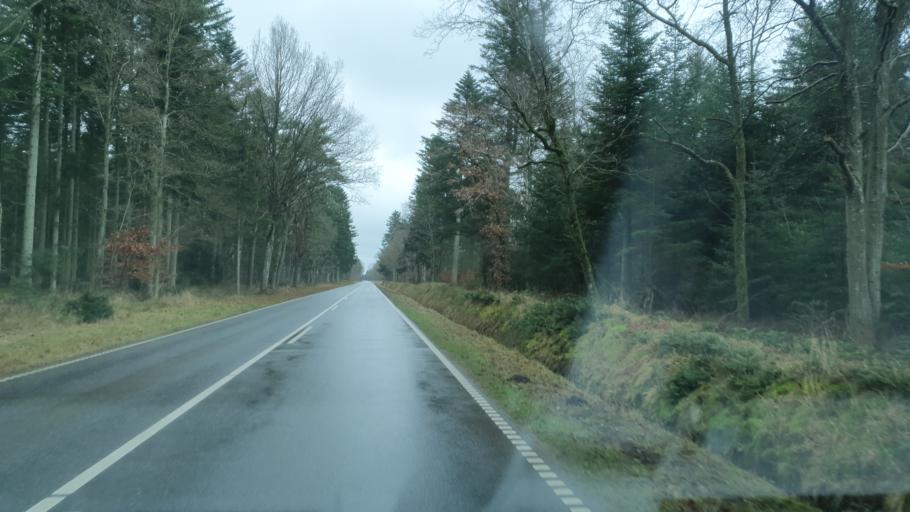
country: DK
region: North Denmark
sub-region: Jammerbugt Kommune
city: Fjerritslev
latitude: 57.1209
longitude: 9.1267
